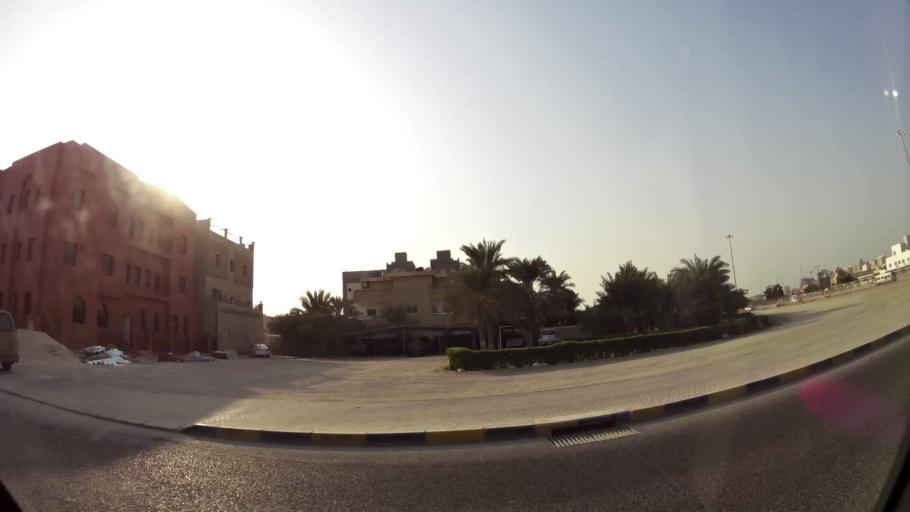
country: KW
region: Muhafazat Hawalli
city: As Salimiyah
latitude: 29.3244
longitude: 48.0828
